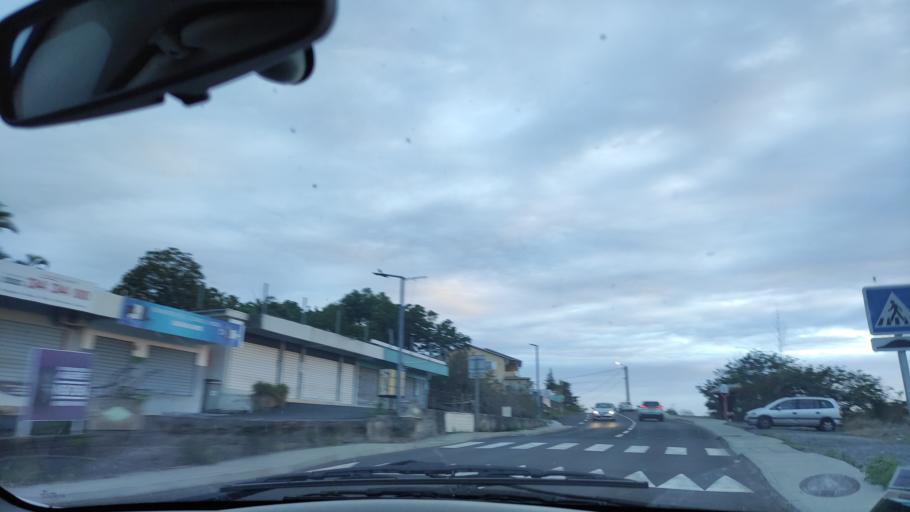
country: RE
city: Piton Saint-Leu
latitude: -21.2073
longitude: 55.2972
